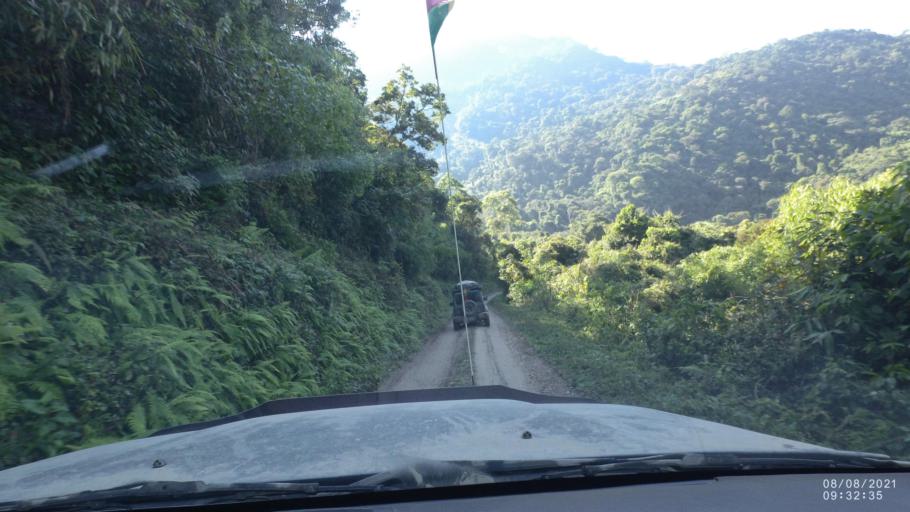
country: BO
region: La Paz
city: Quime
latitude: -16.5884
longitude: -66.7044
